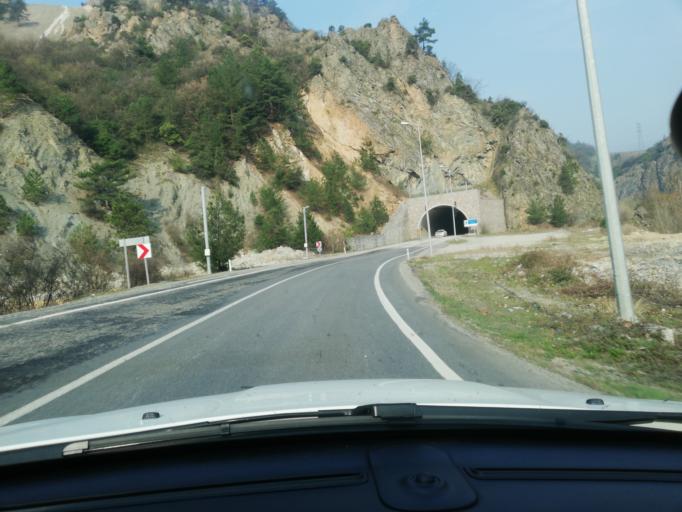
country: TR
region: Karabuk
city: Karabuk
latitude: 41.1517
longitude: 32.5305
